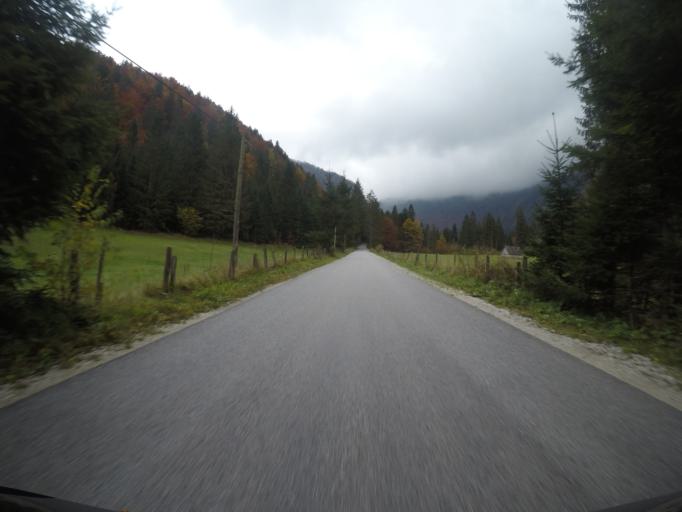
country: SI
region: Jesenice
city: Hrusica
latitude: 46.4083
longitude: 13.9978
